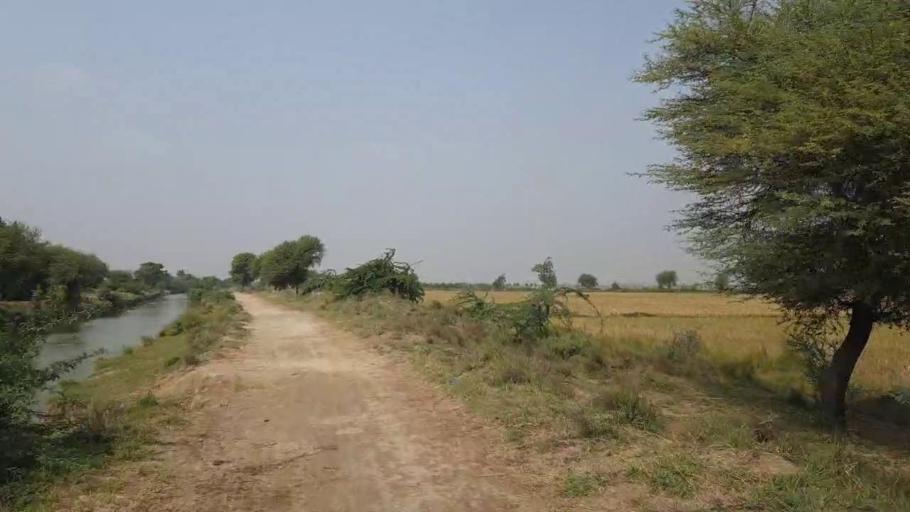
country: PK
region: Sindh
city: Kario
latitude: 24.8460
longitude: 68.5357
